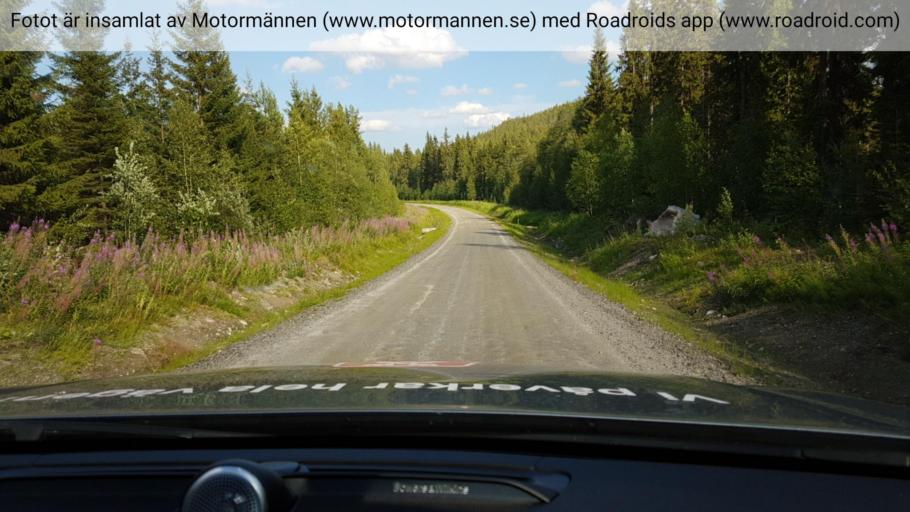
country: SE
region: Vaesterbotten
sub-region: Dorotea Kommun
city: Dorotea
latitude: 63.9192
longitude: 16.2151
